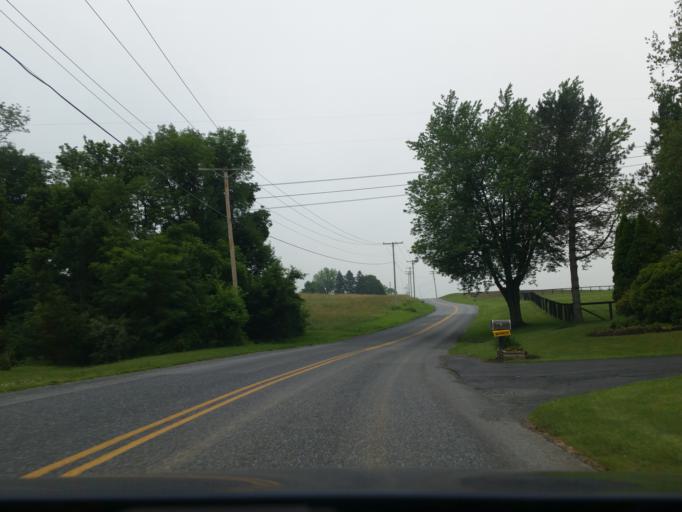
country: US
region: Pennsylvania
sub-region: Lebanon County
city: Palmyra
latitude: 40.3885
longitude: -76.6377
